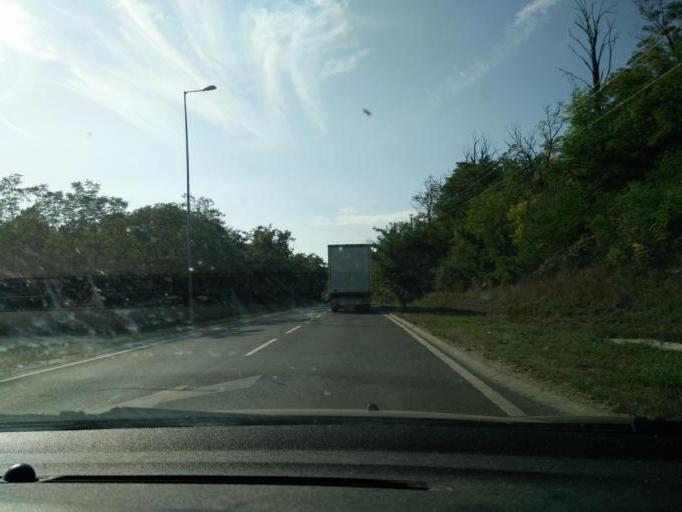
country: HU
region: Pest
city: Pilisszentivan
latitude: 47.6201
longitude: 18.8769
